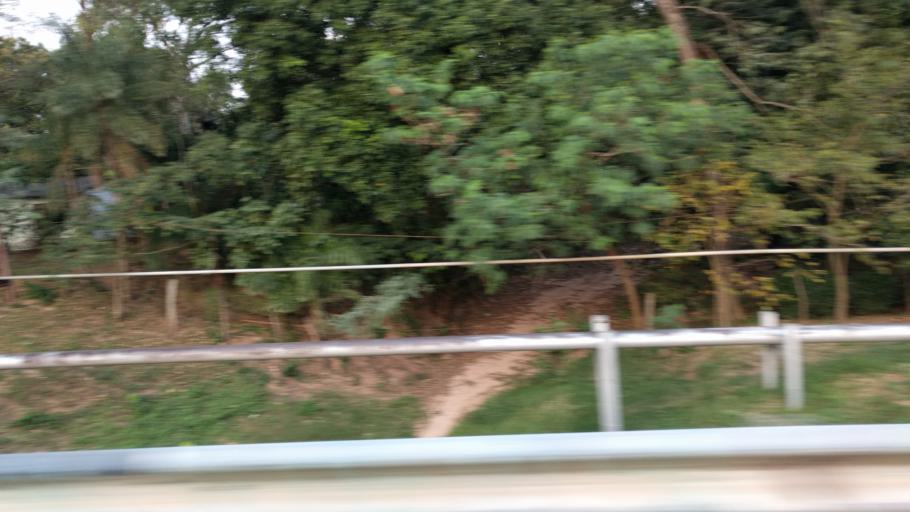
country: BO
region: Santa Cruz
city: Santa Rita
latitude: -17.9702
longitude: -63.3637
